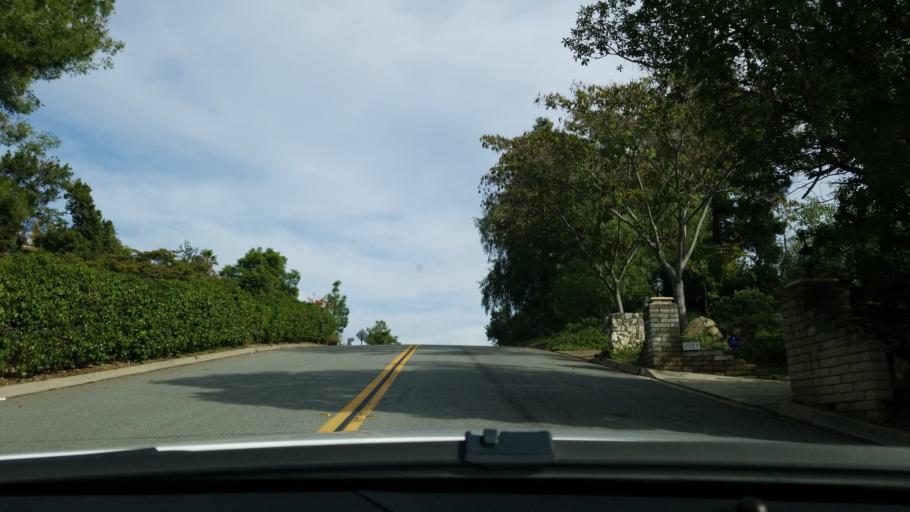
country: US
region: California
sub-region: San Diego County
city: Casa de Oro-Mount Helix
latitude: 32.7678
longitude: -116.9523
